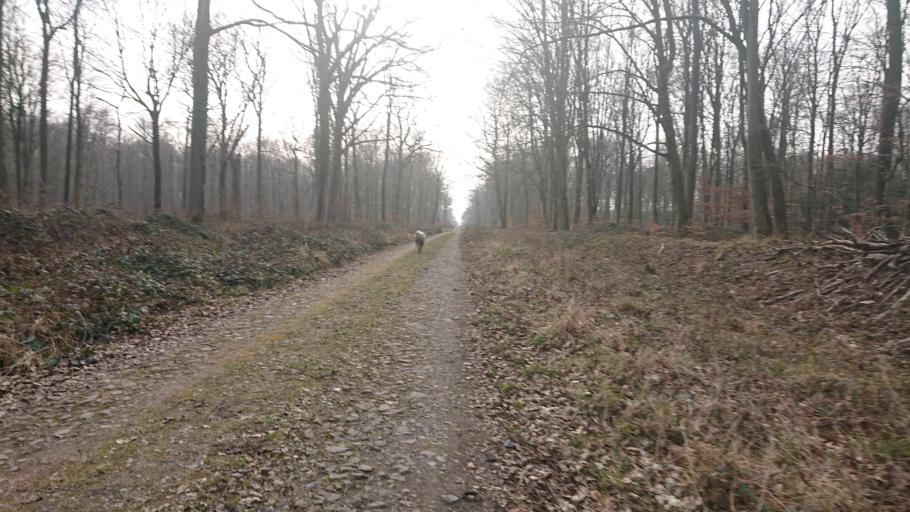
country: FR
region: Nord-Pas-de-Calais
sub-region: Departement du Nord
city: Landrecies
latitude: 50.1661
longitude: 3.7070
